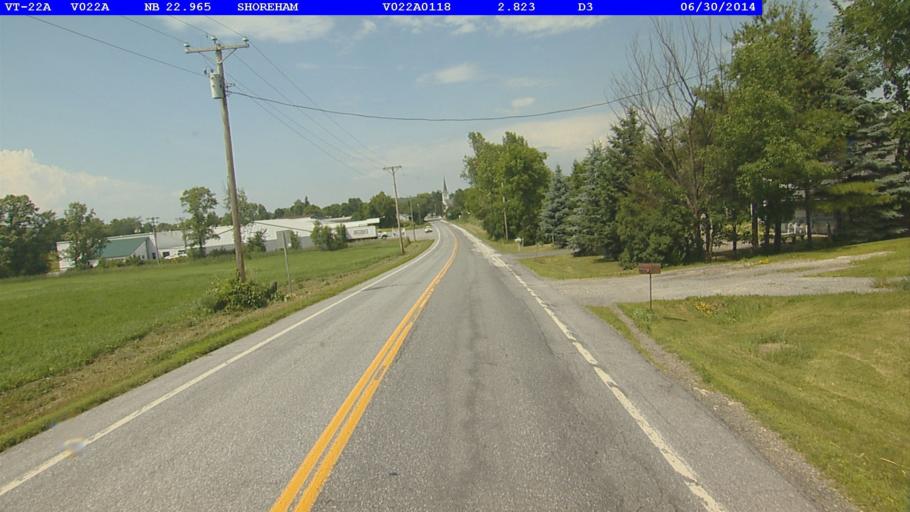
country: US
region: New York
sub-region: Essex County
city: Ticonderoga
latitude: 43.8902
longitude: -73.3095
